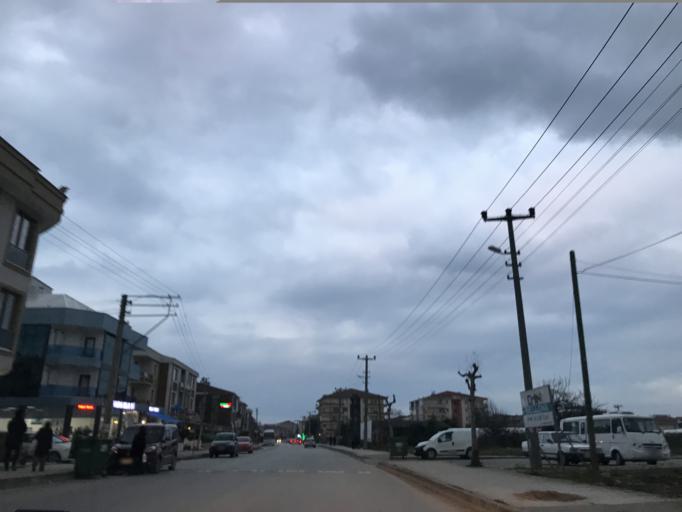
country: TR
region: Yalova
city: Yalova
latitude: 40.6434
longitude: 29.2595
